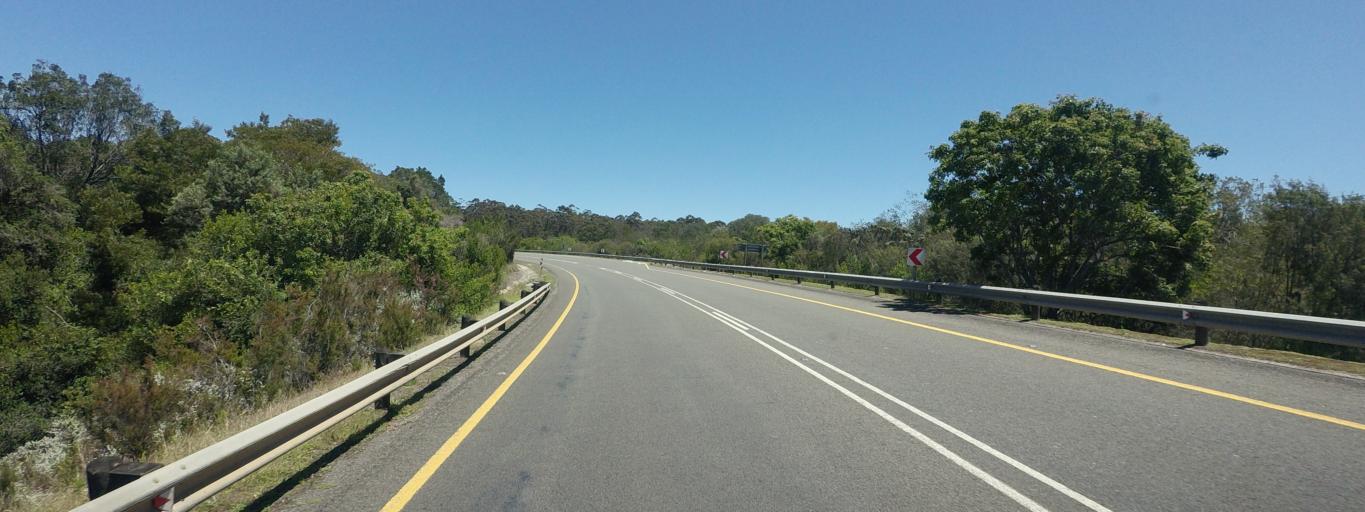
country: ZA
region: Western Cape
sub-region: Eden District Municipality
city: Plettenberg Bay
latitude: -33.9687
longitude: 23.4417
